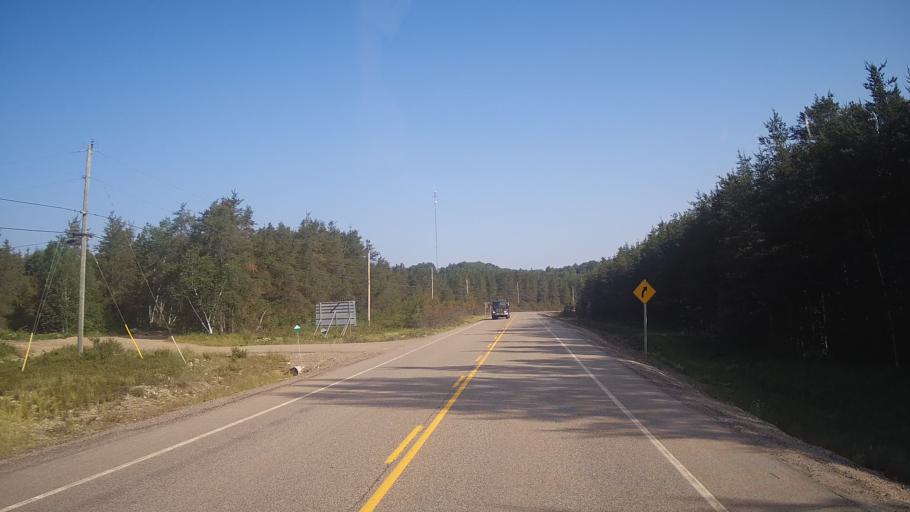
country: CA
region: Ontario
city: Rayside-Balfour
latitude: 46.7057
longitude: -81.5597
